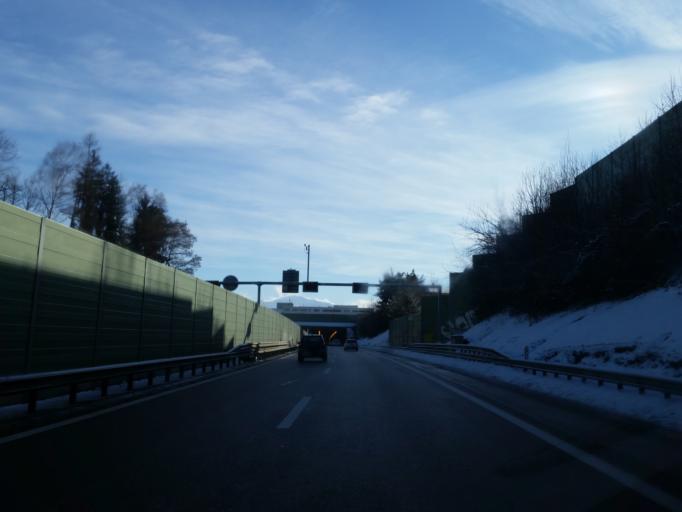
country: CH
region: Schwyz
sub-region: Bezirk March
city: Altendorf
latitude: 47.1914
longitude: 8.8218
